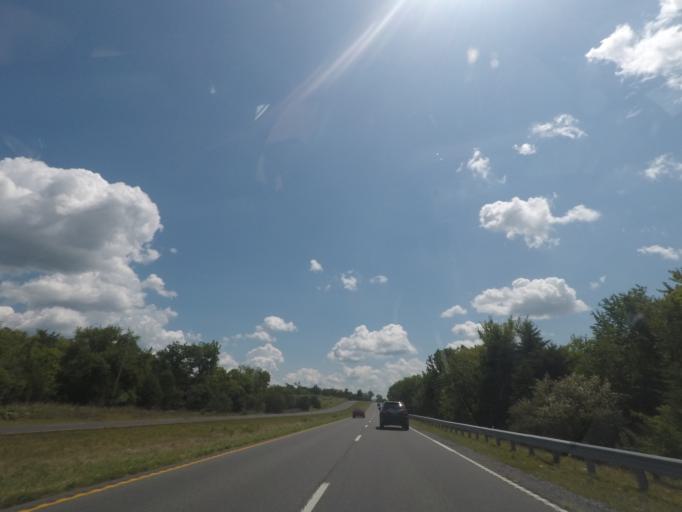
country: US
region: Virginia
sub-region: City of Winchester
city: Winchester
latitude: 39.0956
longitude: -78.1053
